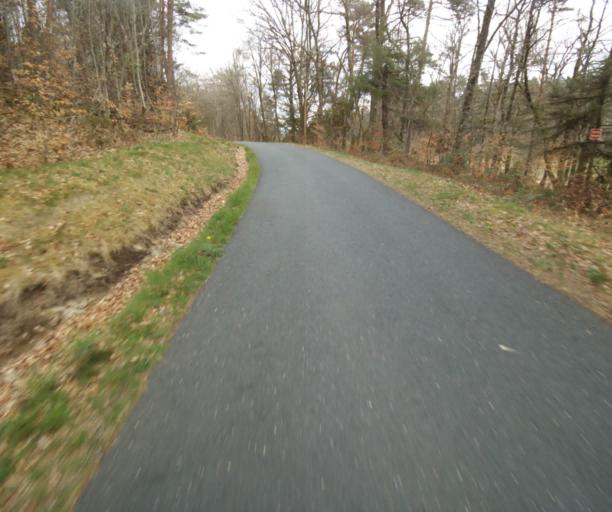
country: FR
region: Limousin
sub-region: Departement de la Correze
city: Correze
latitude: 45.3004
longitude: 1.9144
